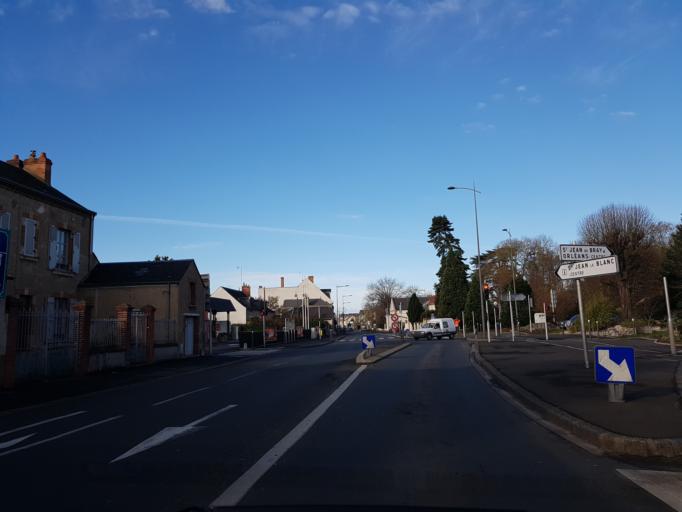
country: FR
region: Centre
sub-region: Departement du Loiret
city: Saint-Jean-le-Blanc
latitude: 47.8900
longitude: 1.9230
